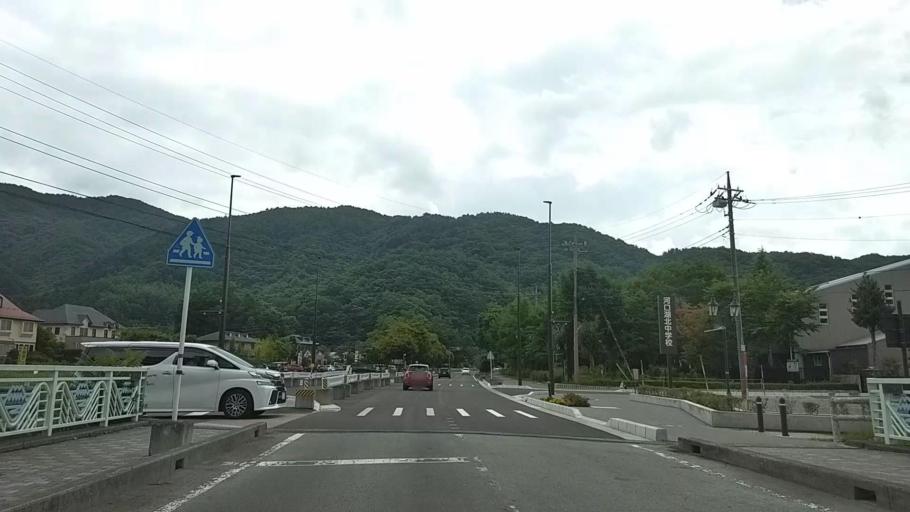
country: JP
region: Yamanashi
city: Fujikawaguchiko
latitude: 35.5219
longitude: 138.7700
